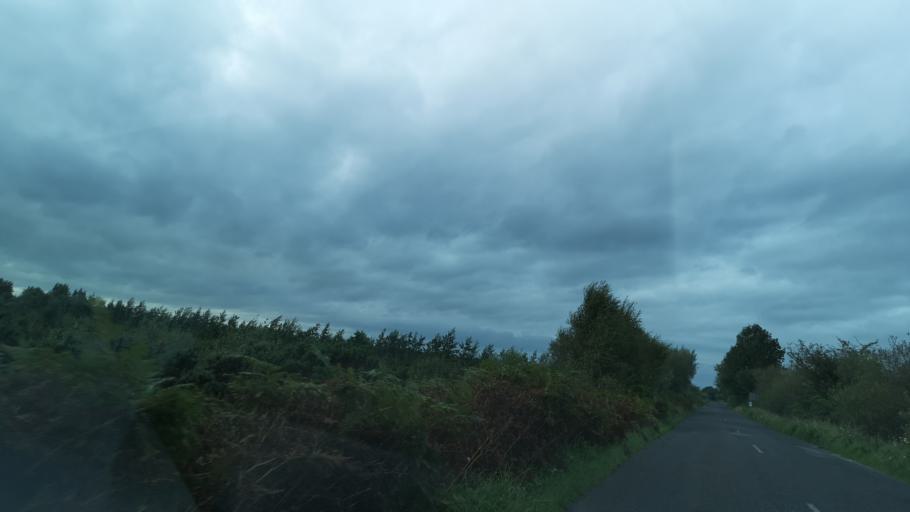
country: IE
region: Leinster
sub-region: Uibh Fhaili
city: Ferbane
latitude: 53.2112
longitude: -7.7886
